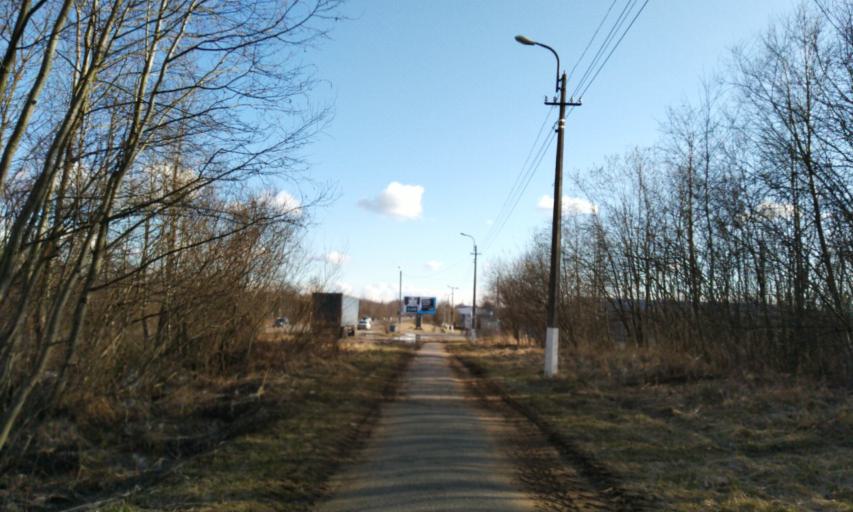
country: RU
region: Leningrad
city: Novoye Devyatkino
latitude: 60.1054
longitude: 30.4994
